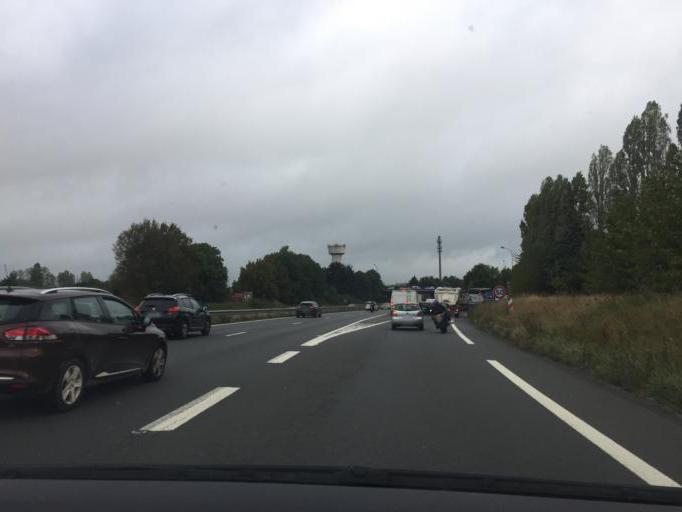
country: FR
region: Ile-de-France
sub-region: Departement de l'Essonne
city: Saclay
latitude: 48.7270
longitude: 2.1660
